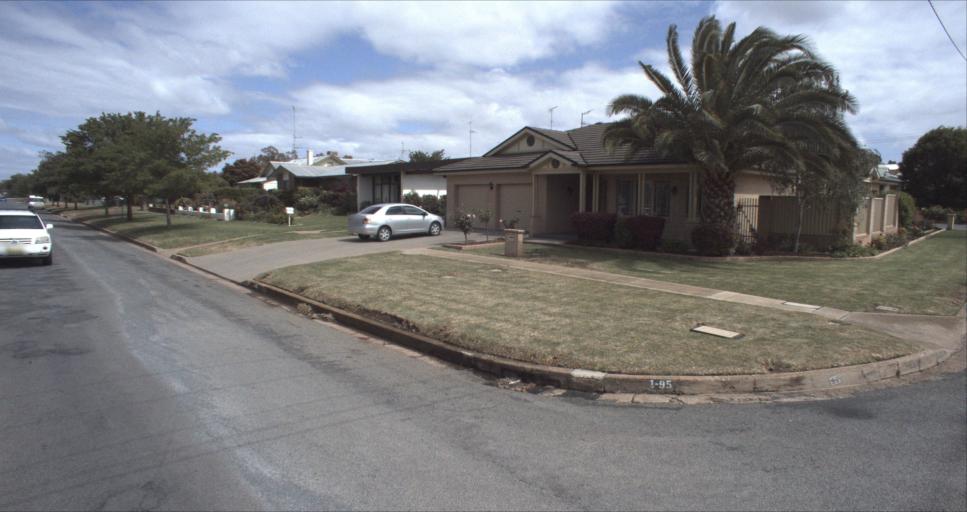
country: AU
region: New South Wales
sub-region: Leeton
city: Leeton
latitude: -34.5574
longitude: 146.4064
